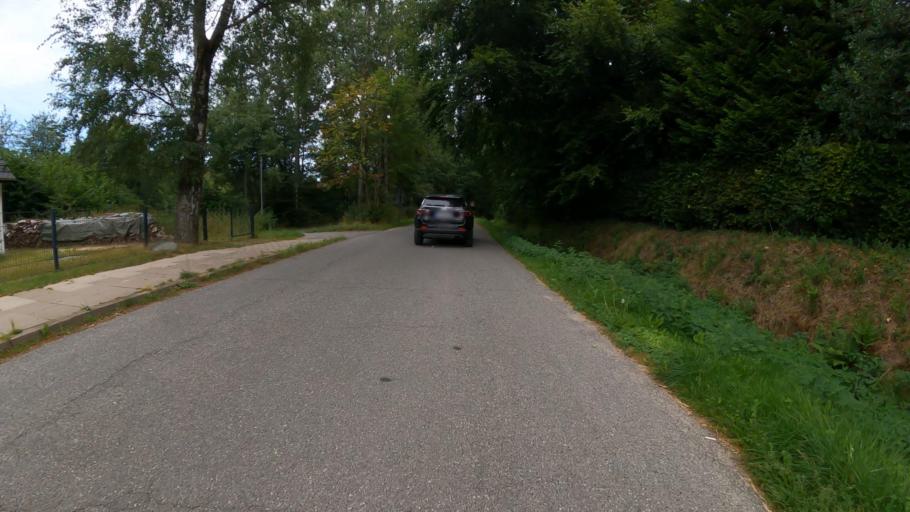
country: DE
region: Lower Saxony
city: Bendestorf
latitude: 53.3519
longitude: 9.9215
